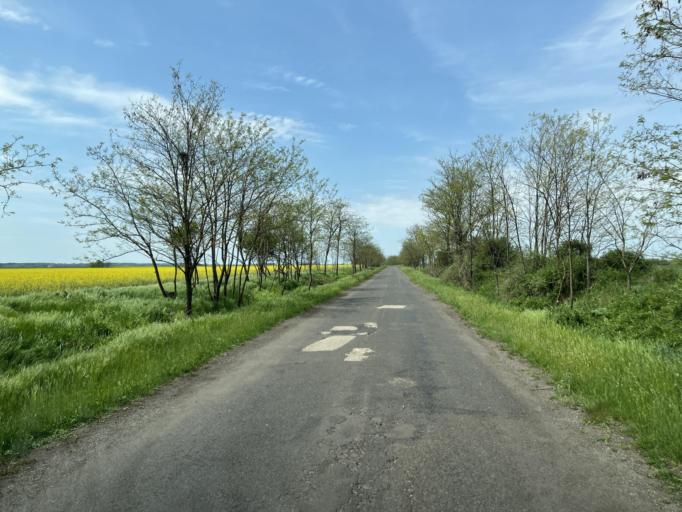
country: HU
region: Pest
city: Tapiogyorgye
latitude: 47.2954
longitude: 19.9927
